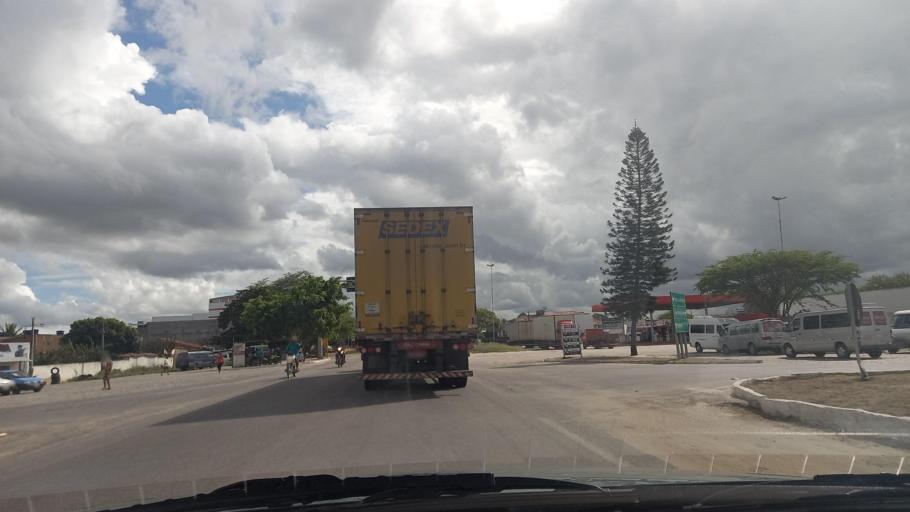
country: BR
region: Pernambuco
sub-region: Lajedo
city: Lajedo
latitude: -8.6586
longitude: -36.3311
